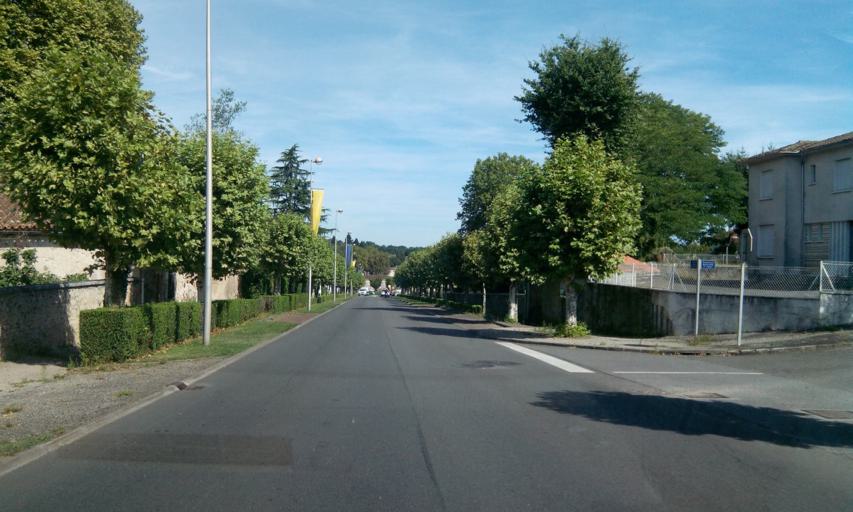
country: FR
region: Poitou-Charentes
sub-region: Departement de la Charente
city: Confolens
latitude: 46.0088
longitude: 0.6719
